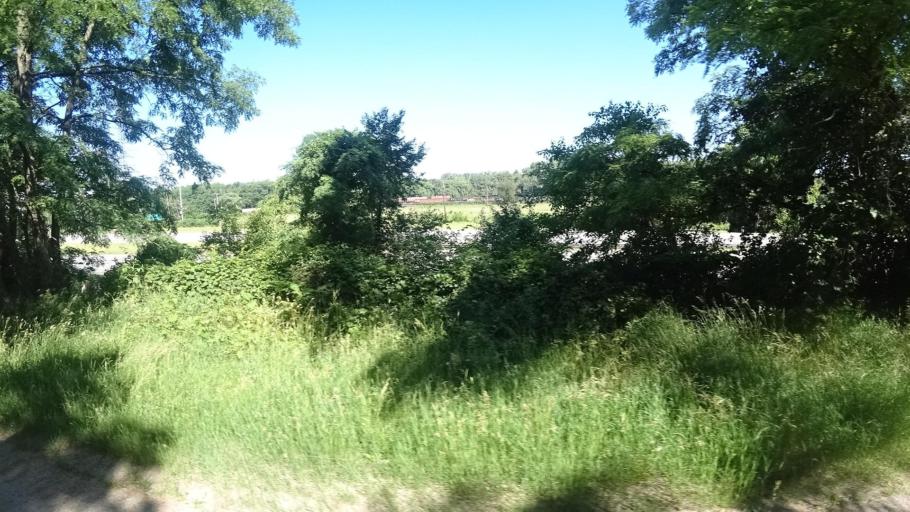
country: US
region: Indiana
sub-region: Porter County
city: Burns Harbor
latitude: 41.6267
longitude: -87.1131
